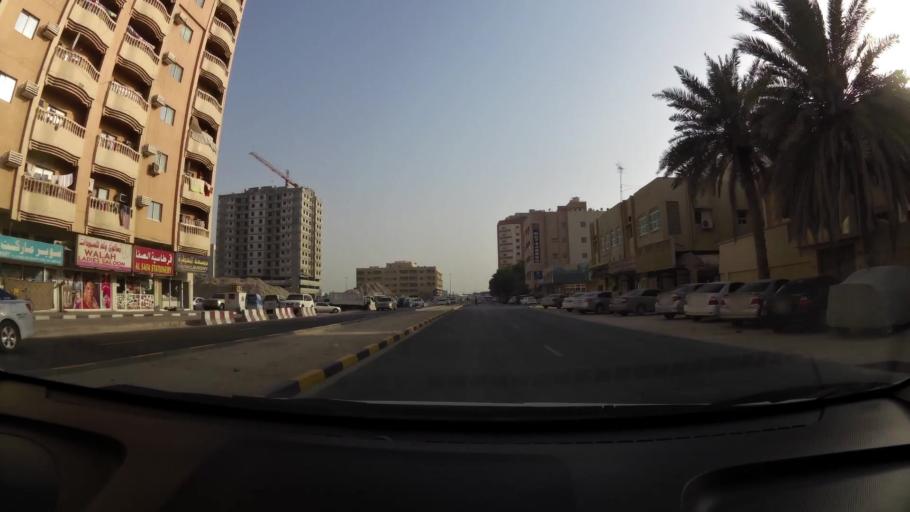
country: AE
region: Ajman
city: Ajman
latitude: 25.3790
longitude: 55.4574
